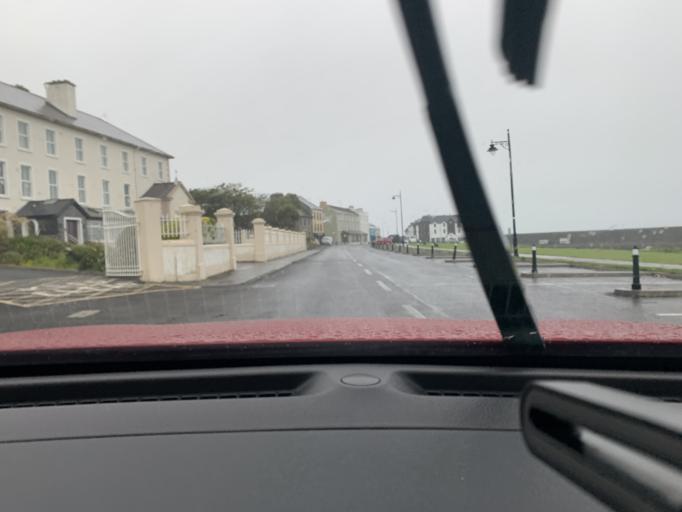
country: IE
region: Connaught
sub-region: County Leitrim
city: Kinlough
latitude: 54.4653
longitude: -8.4498
